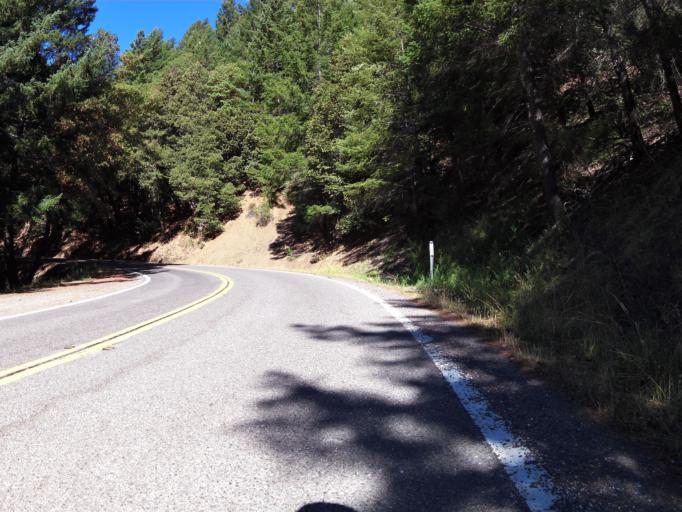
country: US
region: California
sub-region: Humboldt County
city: Redway
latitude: 39.8530
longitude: -123.7417
